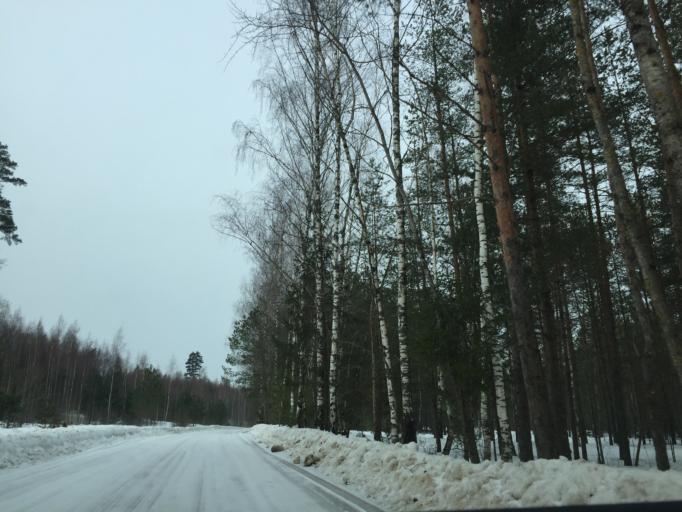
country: LV
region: Ogre
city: Ogre
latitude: 56.8398
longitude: 24.5702
